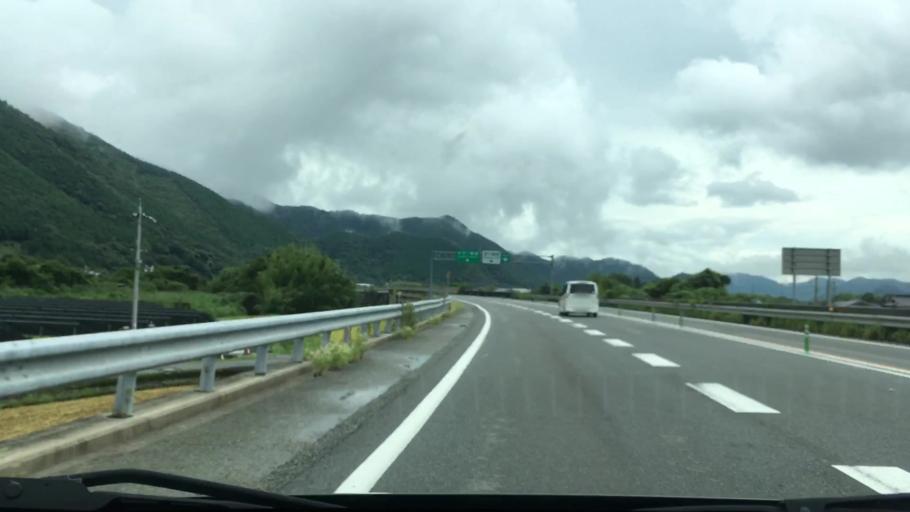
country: JP
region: Hyogo
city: Yamazakicho-nakabirose
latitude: 35.0506
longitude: 134.7640
